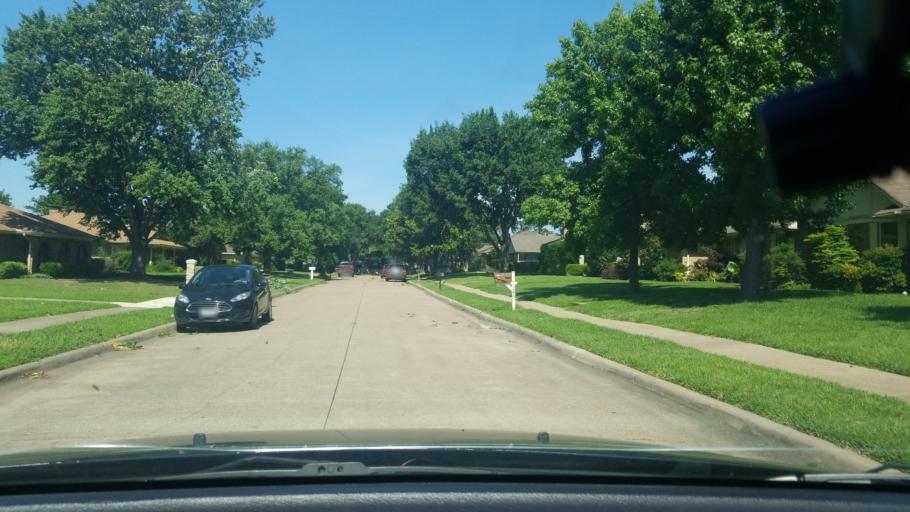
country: US
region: Texas
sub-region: Dallas County
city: Mesquite
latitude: 32.7718
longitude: -96.5924
